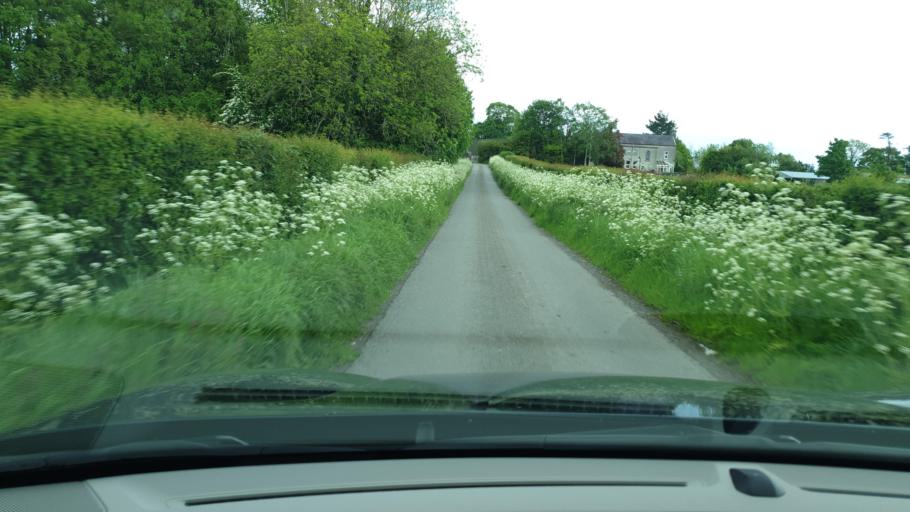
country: IE
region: Leinster
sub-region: An Mhi
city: Ratoath
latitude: 53.5273
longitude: -6.4665
